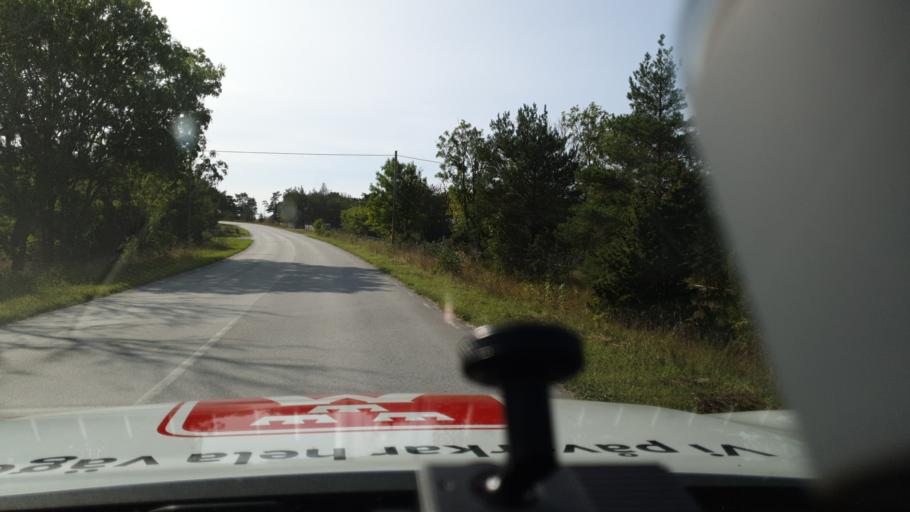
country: SE
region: Gotland
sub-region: Gotland
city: Slite
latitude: 57.9015
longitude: 19.0950
